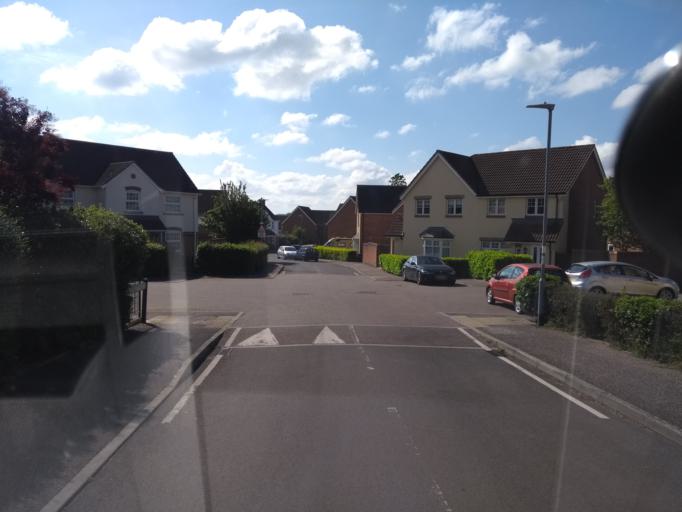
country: GB
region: England
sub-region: Somerset
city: Taunton
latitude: 51.0338
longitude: -3.0847
